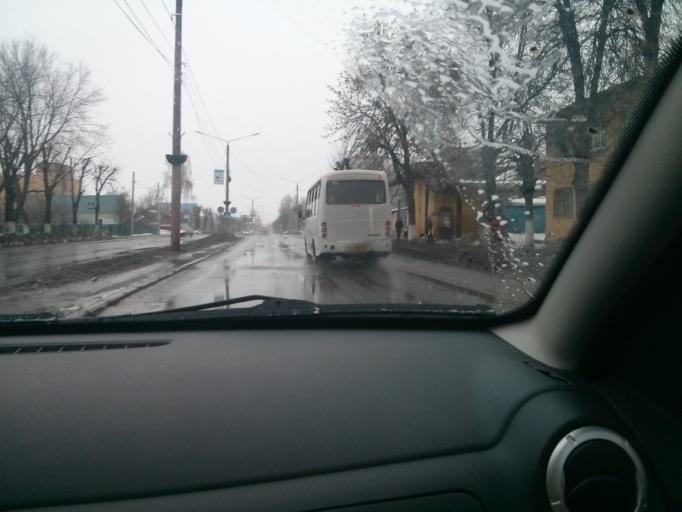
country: RU
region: Vladimir
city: Murom
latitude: 55.5777
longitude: 42.0356
